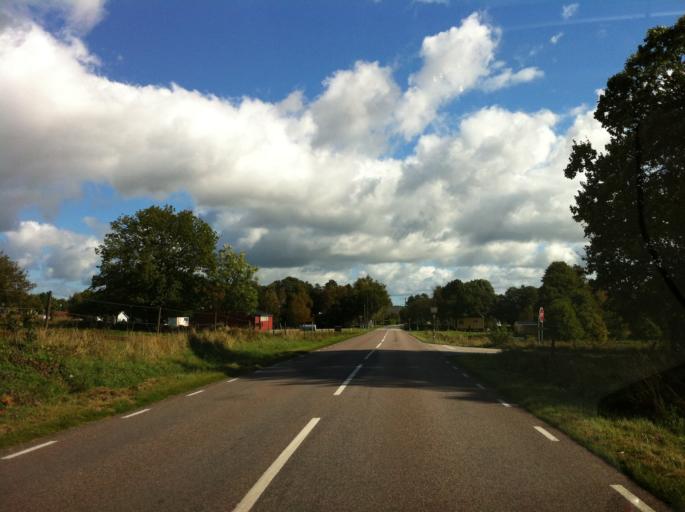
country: SE
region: Skane
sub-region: Horby Kommun
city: Hoerby
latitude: 55.7865
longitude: 13.8543
